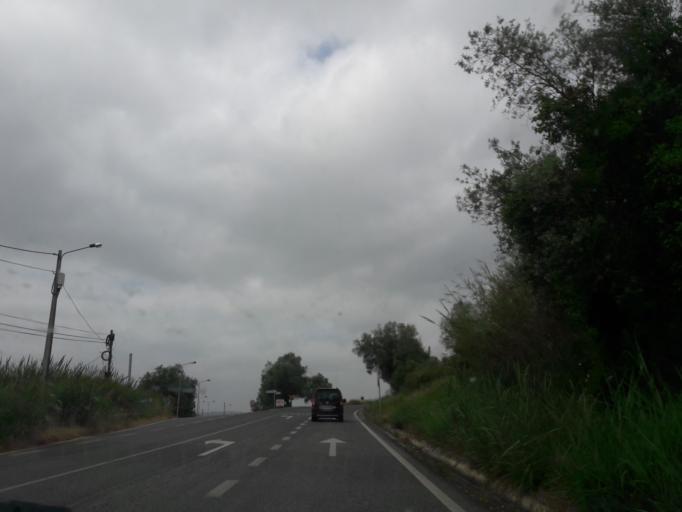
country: PT
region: Leiria
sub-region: Obidos
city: Obidos
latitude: 39.3443
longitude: -9.1952
